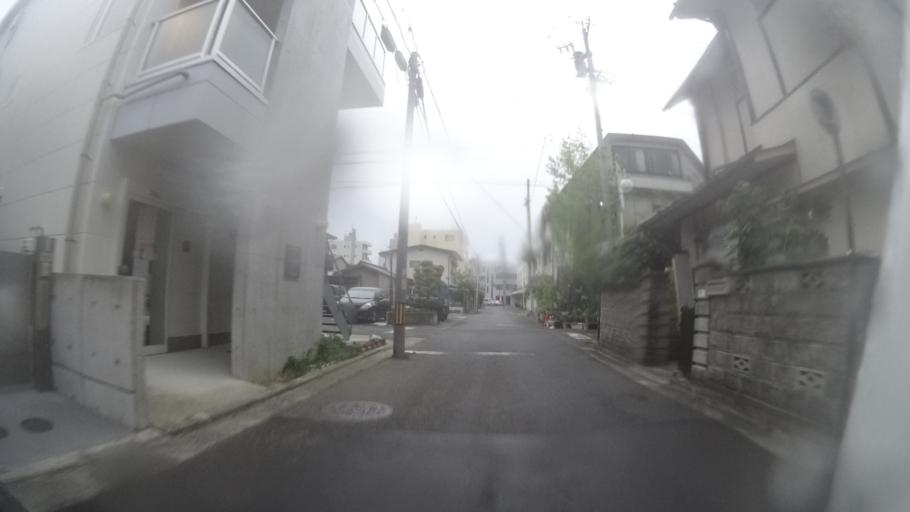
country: JP
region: Nagano
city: Nagano-shi
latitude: 36.6530
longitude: 138.1999
